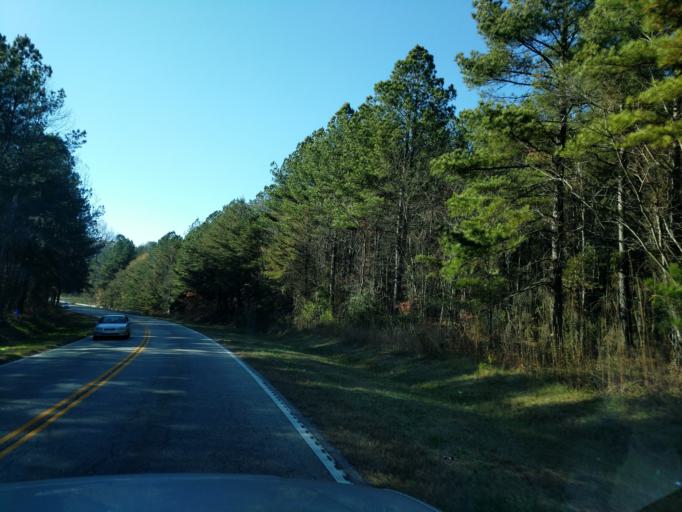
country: US
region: South Carolina
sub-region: Spartanburg County
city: Landrum
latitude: 35.1272
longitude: -82.1328
